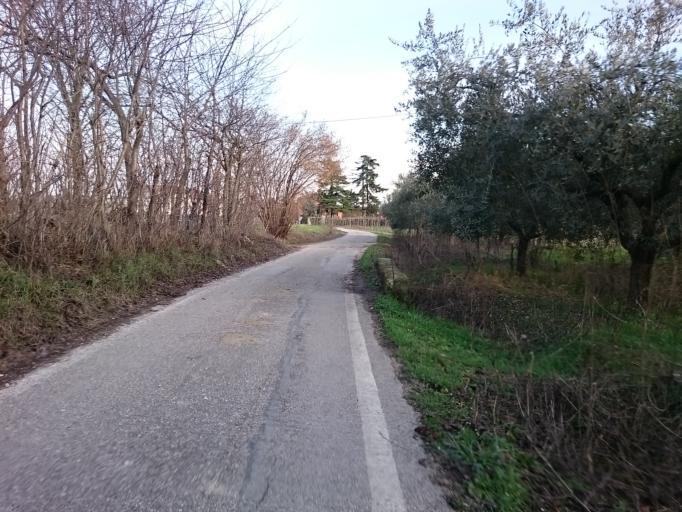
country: IT
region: Veneto
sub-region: Provincia di Verona
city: Cavalcaselle
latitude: 45.4563
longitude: 10.7233
